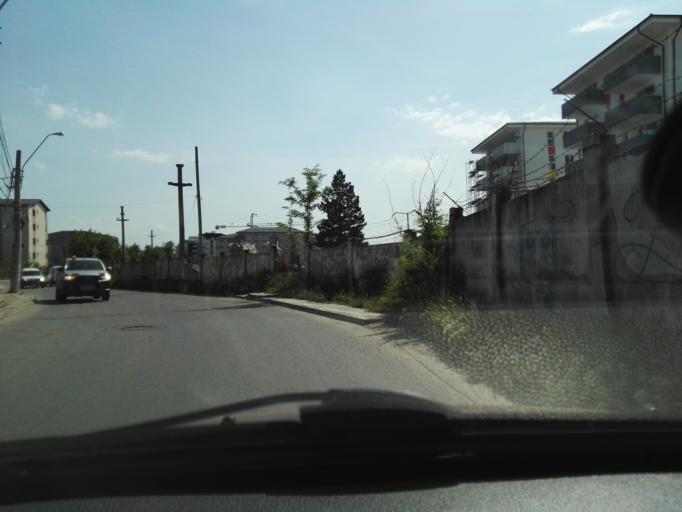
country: RO
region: Ilfov
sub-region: Comuna Popesti-Leordeni
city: Popesti-Leordeni
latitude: 44.3729
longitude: 26.1292
